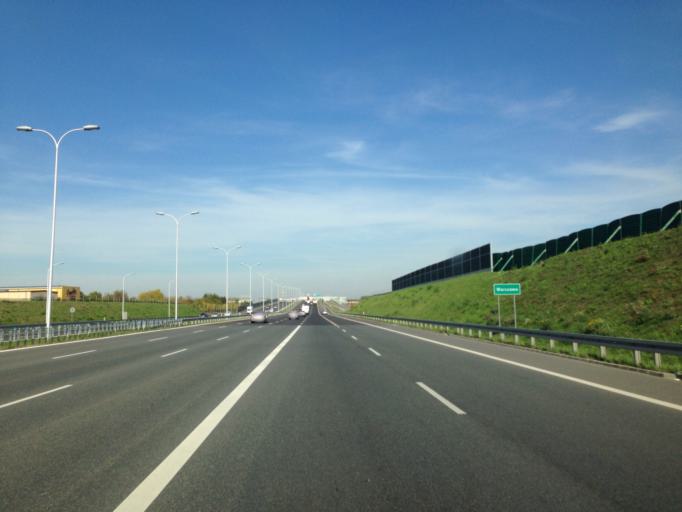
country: PL
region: Masovian Voivodeship
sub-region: Powiat pruszkowski
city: Nowe Grocholice
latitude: 52.1781
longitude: 20.9145
